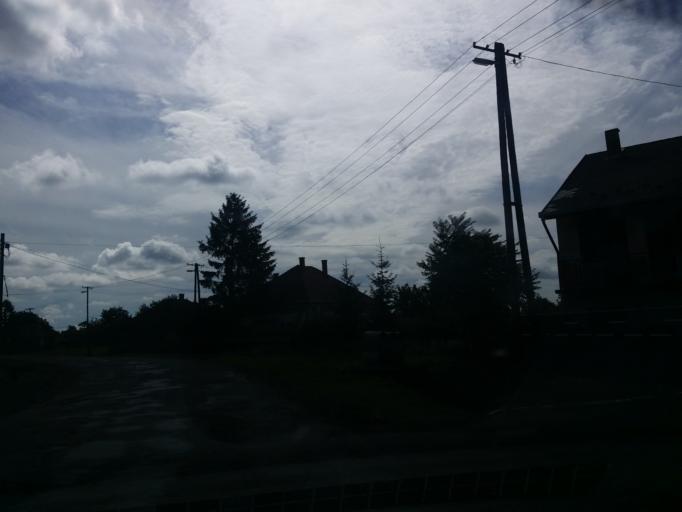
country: HU
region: Heves
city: Erdotelek
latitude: 47.6164
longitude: 20.3653
